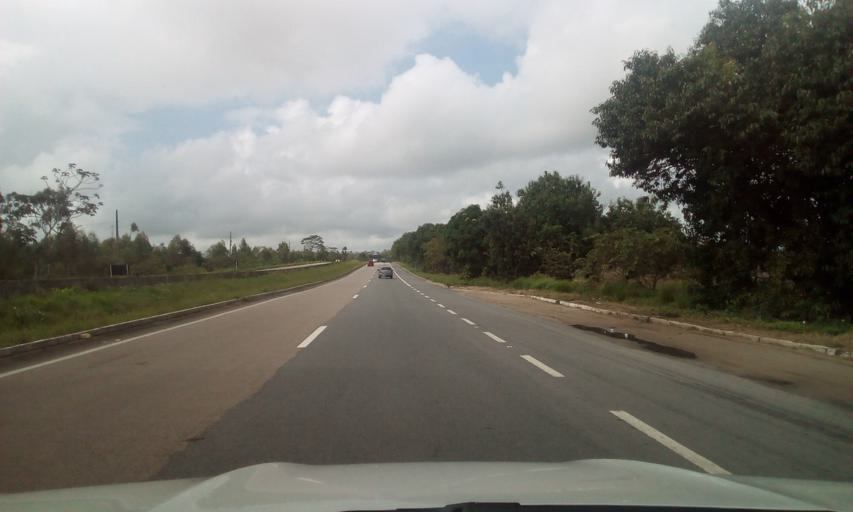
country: BR
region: Paraiba
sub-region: Conde
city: Conde
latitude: -7.2908
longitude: -34.9382
